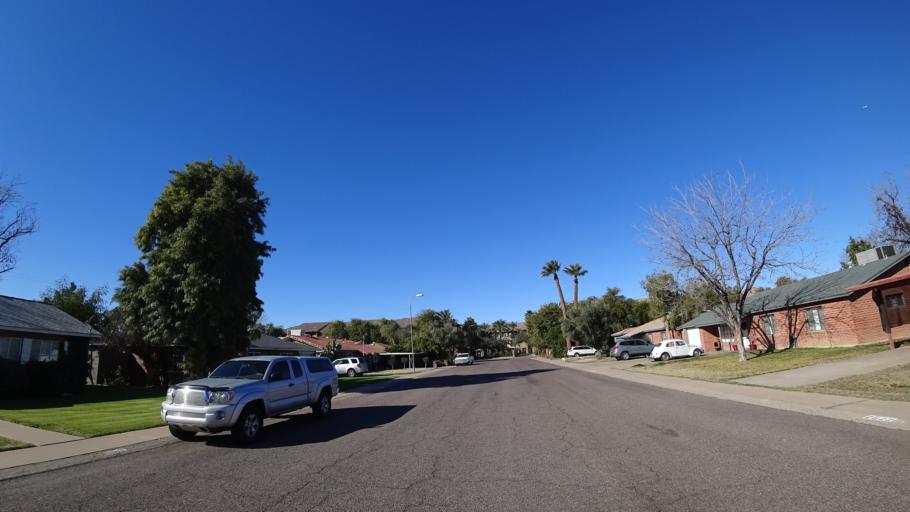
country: US
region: Arizona
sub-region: Maricopa County
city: Phoenix
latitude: 33.5004
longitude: -112.0272
